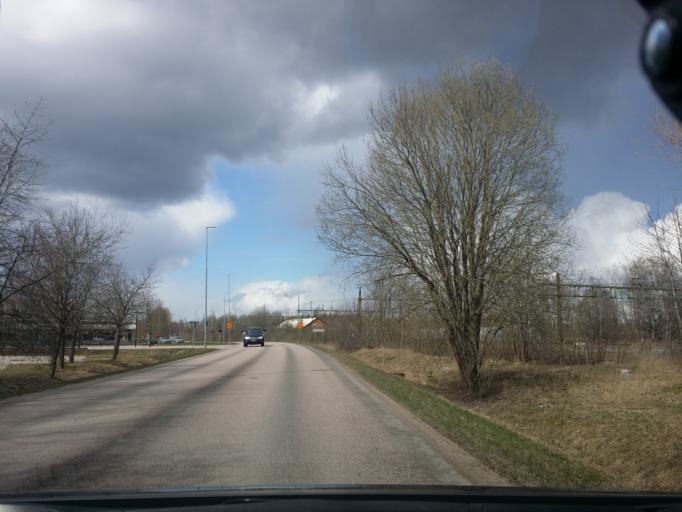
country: SE
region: Vaestmanland
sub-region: Sala Kommun
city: Sala
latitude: 59.9257
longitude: 16.6028
